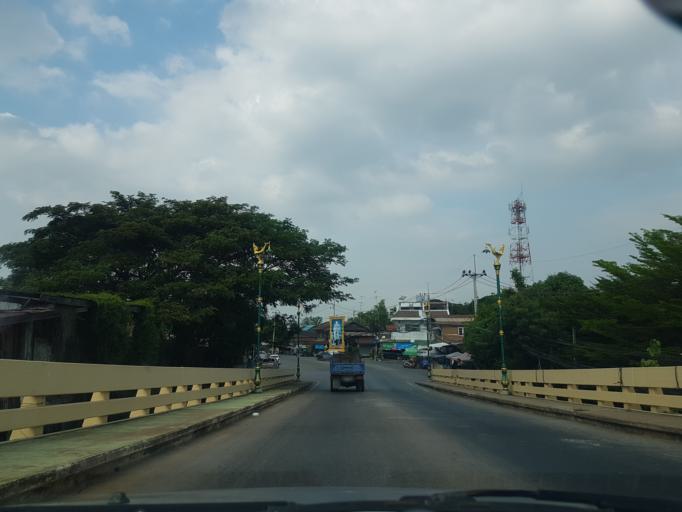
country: TH
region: Phra Nakhon Si Ayutthaya
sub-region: Amphoe Tha Ruea
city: Tha Ruea
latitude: 14.5606
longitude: 100.7199
